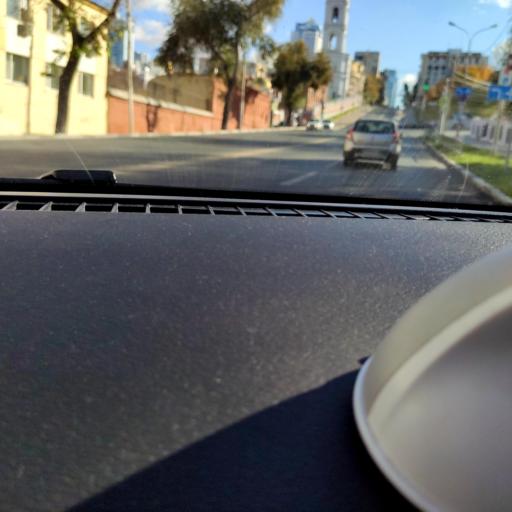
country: RU
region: Samara
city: Rozhdestveno
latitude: 53.1996
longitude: 50.0955
